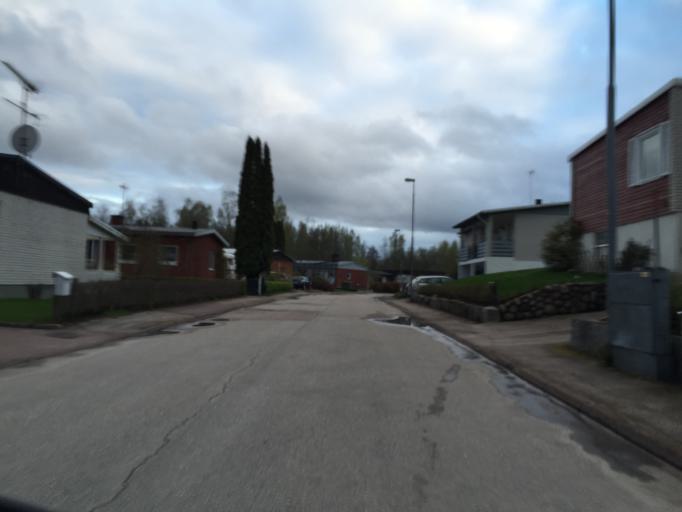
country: SE
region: Dalarna
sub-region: Ludvika Kommun
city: Ludvika
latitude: 60.1387
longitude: 15.2033
